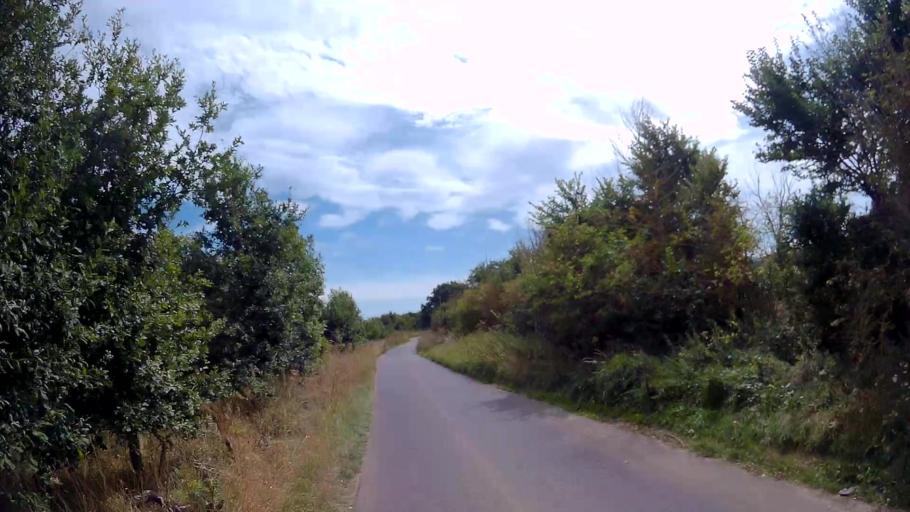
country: GB
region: England
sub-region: Hampshire
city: Odiham
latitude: 51.2330
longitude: -0.9635
